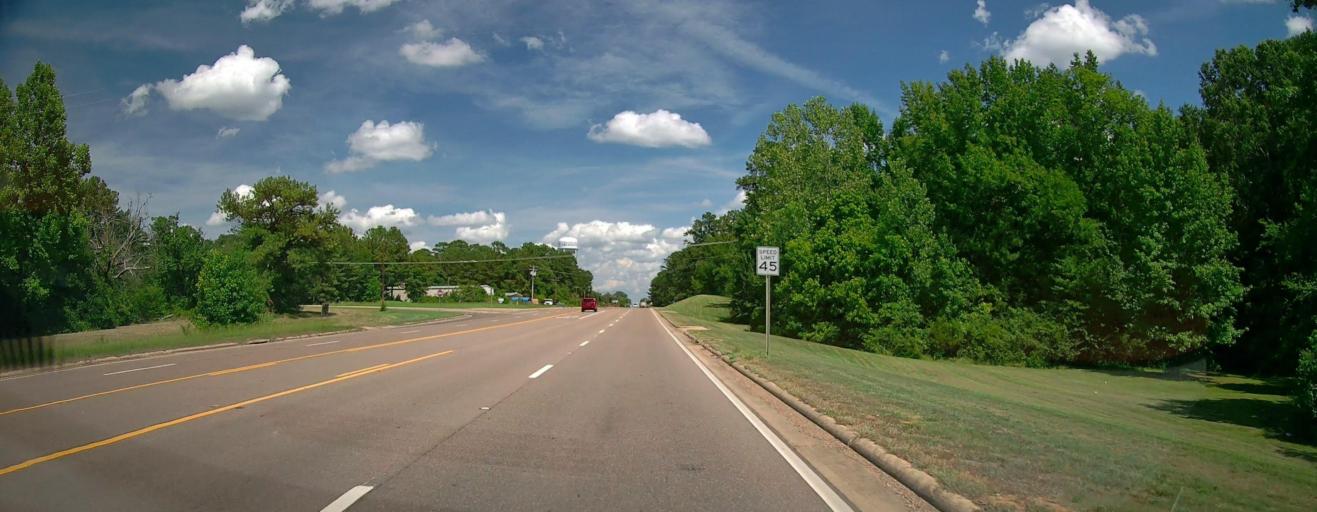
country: US
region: Mississippi
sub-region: Monroe County
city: Aberdeen
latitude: 33.8148
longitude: -88.5630
